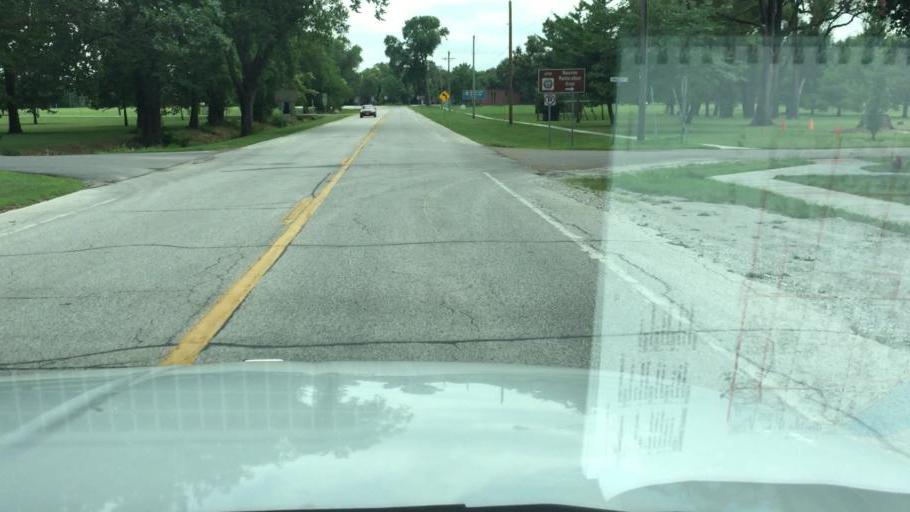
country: US
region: Illinois
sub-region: Hancock County
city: Nauvoo
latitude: 40.5432
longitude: -91.3867
